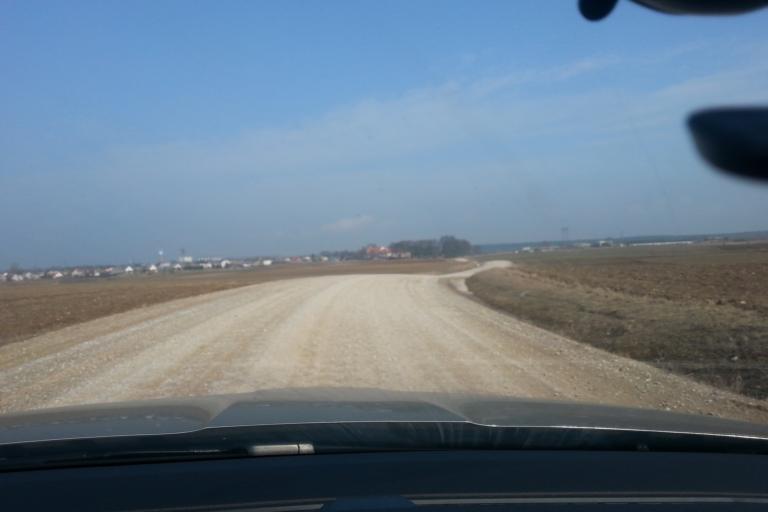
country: LT
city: Trakai
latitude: 54.5982
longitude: 24.9787
